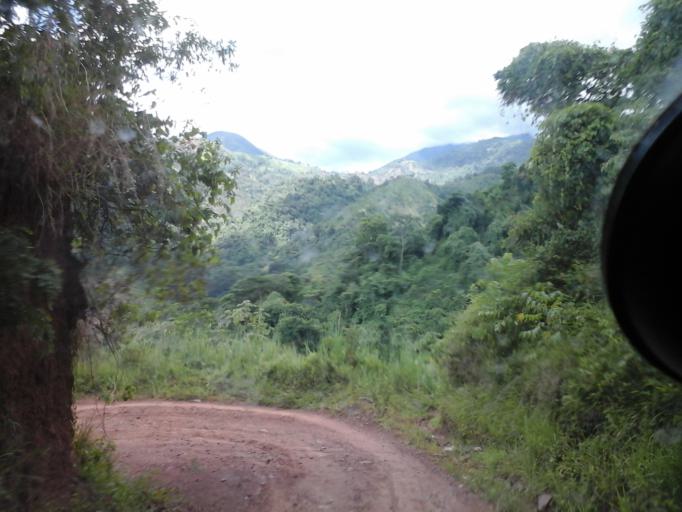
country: CO
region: Cesar
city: San Diego
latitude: 10.2705
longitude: -73.0837
